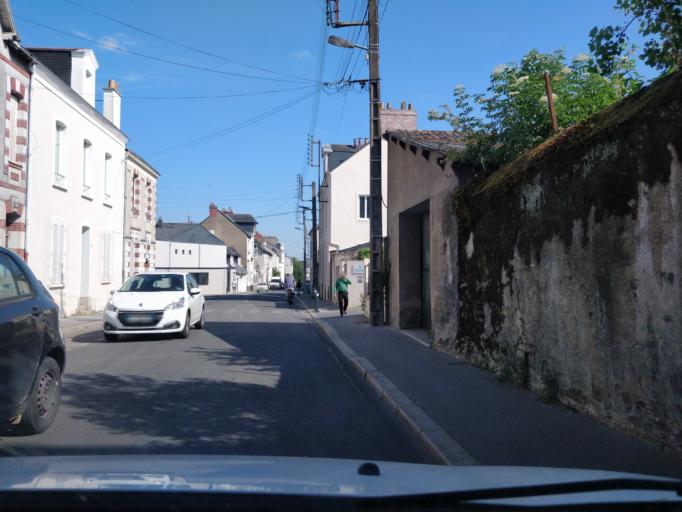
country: FR
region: Pays de la Loire
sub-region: Departement de la Loire-Atlantique
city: Nantes
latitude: 47.2261
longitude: -1.5411
